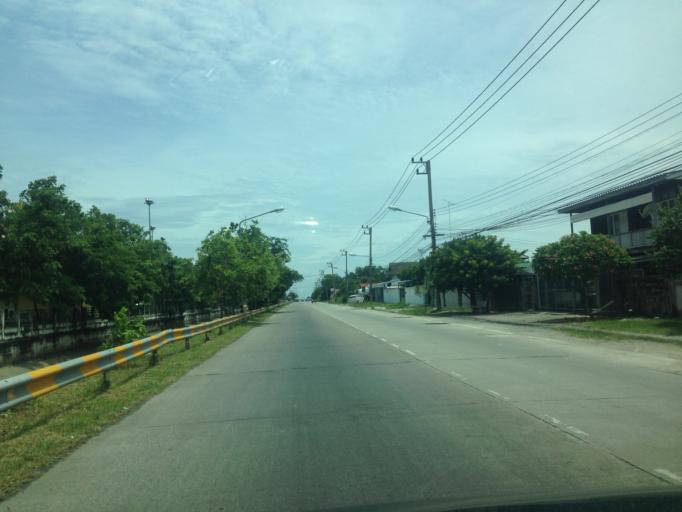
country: TH
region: Chon Buri
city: Chon Buri
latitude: 13.3745
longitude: 100.9836
